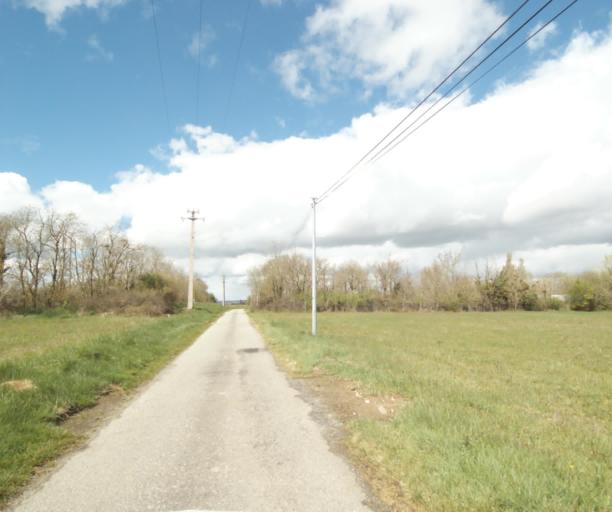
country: FR
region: Midi-Pyrenees
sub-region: Departement de l'Ariege
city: Saverdun
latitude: 43.2583
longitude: 1.5966
